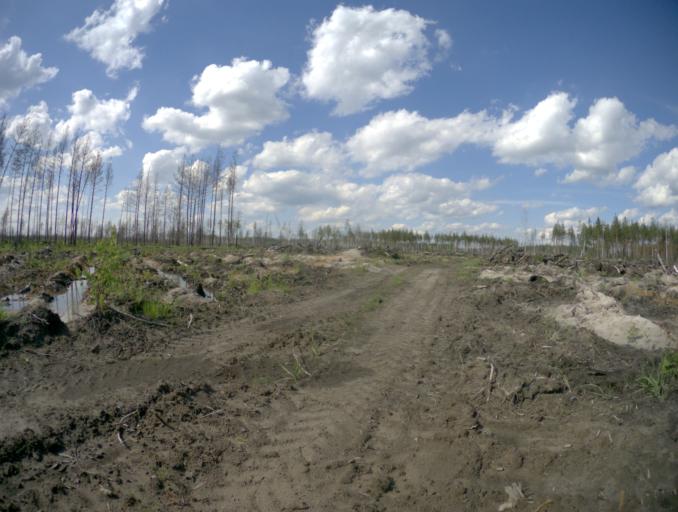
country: RU
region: Vladimir
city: Velikodvorskiy
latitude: 55.3156
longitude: 40.9195
